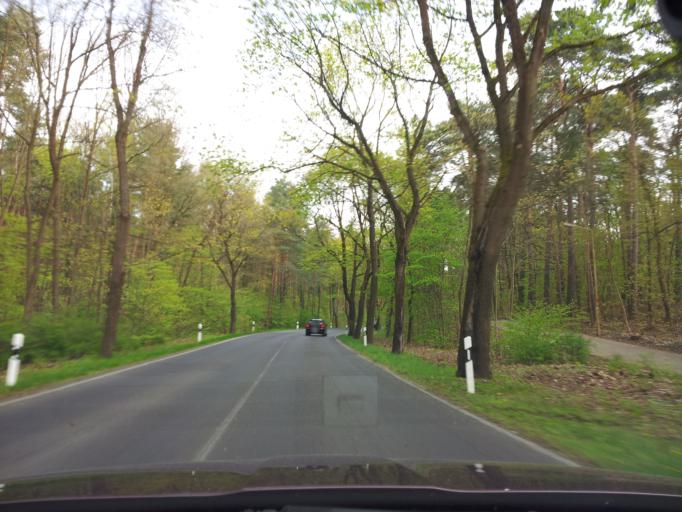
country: DE
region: Brandenburg
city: Grunheide
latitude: 52.4294
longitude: 13.8305
